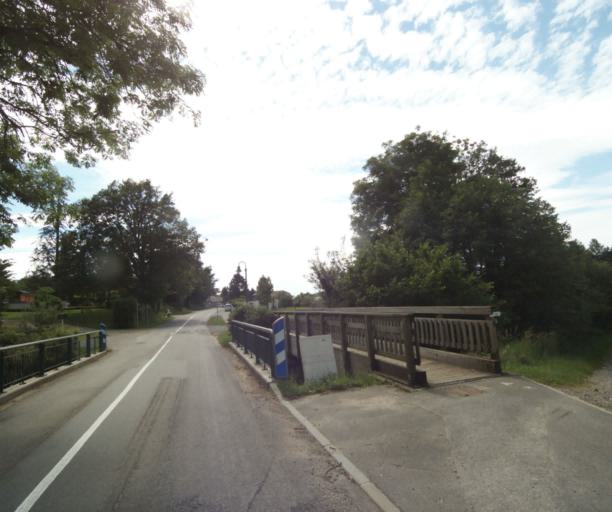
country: FR
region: Rhone-Alpes
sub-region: Departement de la Haute-Savoie
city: Perrignier
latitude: 46.2836
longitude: 6.4372
